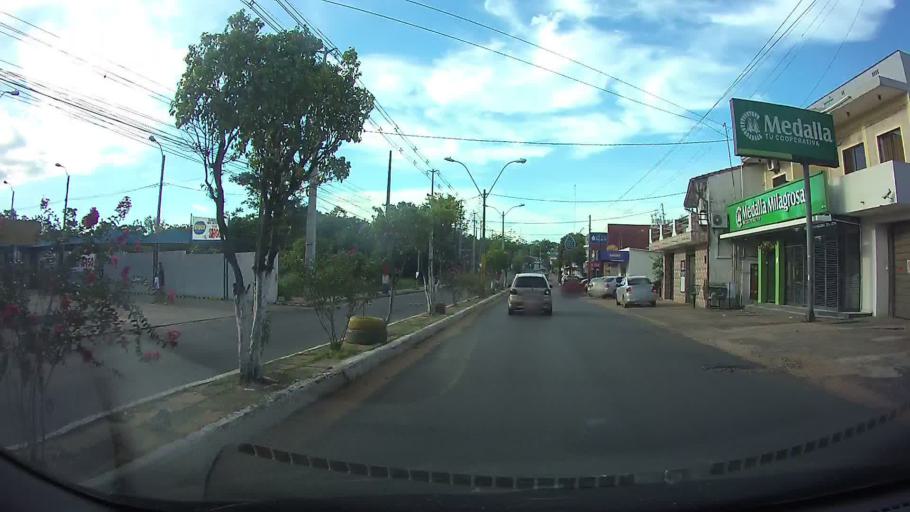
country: PY
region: Central
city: San Antonio
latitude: -25.4156
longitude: -57.5727
